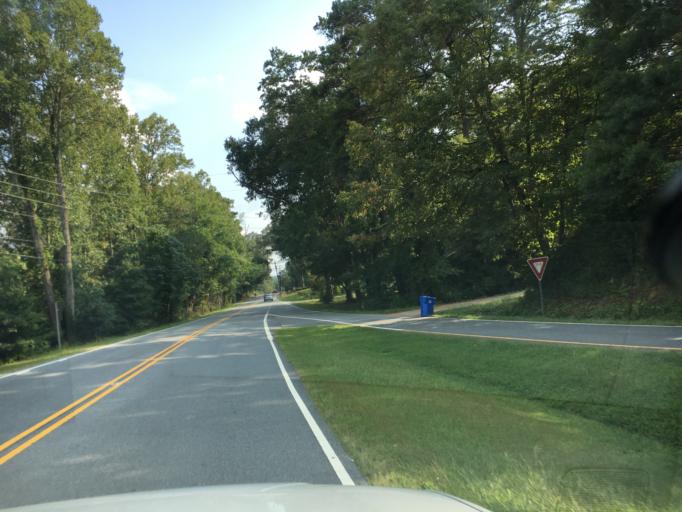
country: US
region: North Carolina
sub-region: Rutherford County
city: Rutherfordton
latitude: 35.3806
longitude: -81.9561
